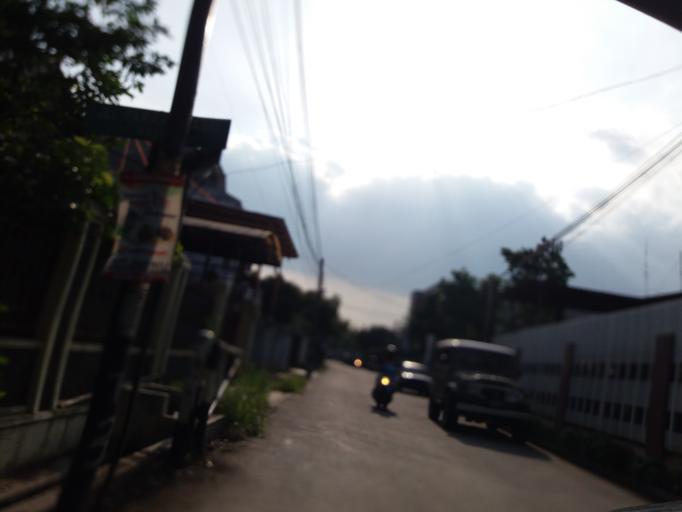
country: ID
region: West Java
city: Bandung
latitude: -6.9527
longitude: 107.6321
